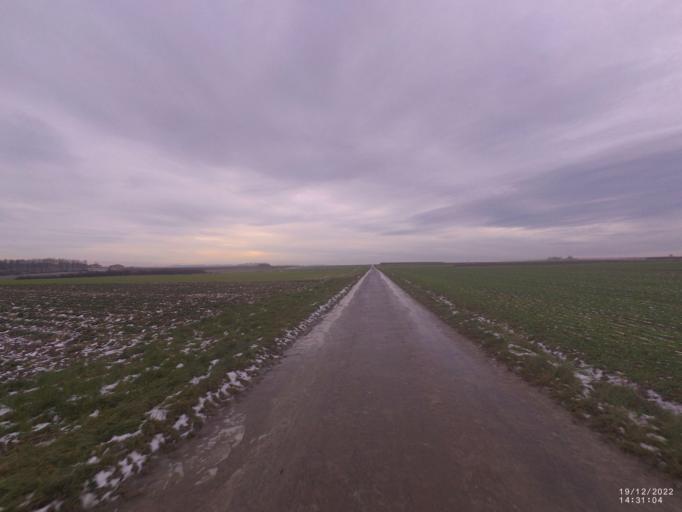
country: DE
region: Rheinland-Pfalz
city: Unkel
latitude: 50.6027
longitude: 7.1578
